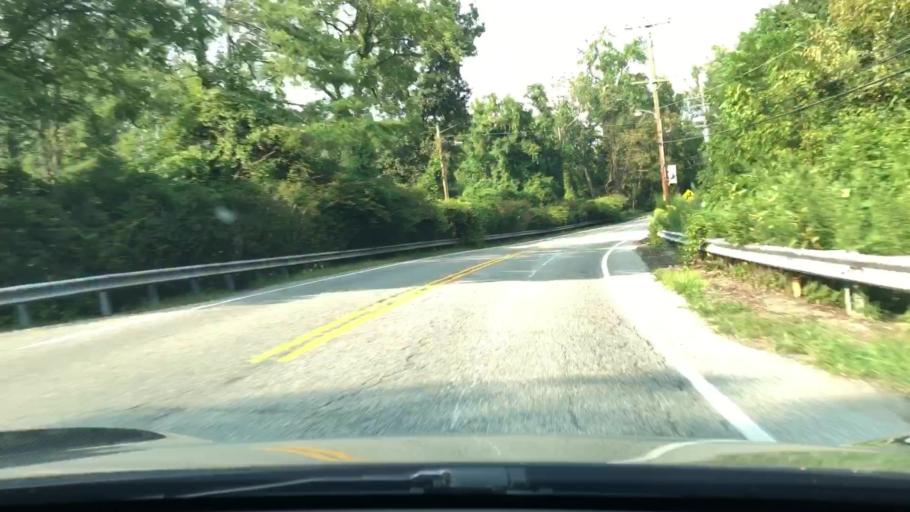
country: US
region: Pennsylvania
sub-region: Delaware County
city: Wayne
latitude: 40.0268
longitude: -75.3962
